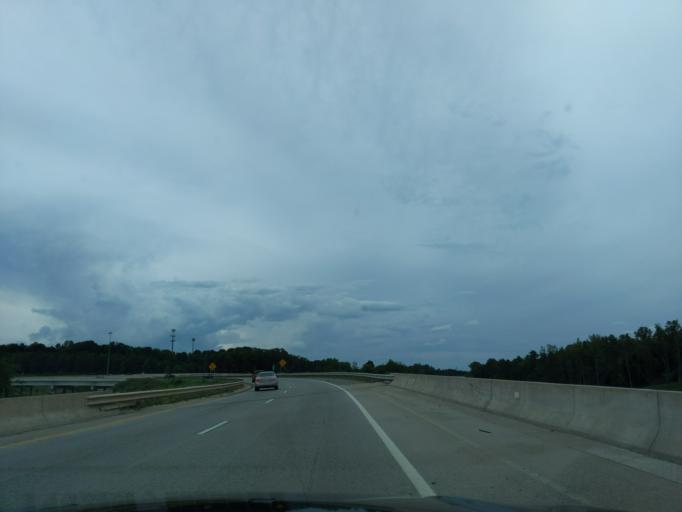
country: US
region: North Carolina
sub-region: Cabarrus County
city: Harrisburg
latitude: 35.3481
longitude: -80.7311
